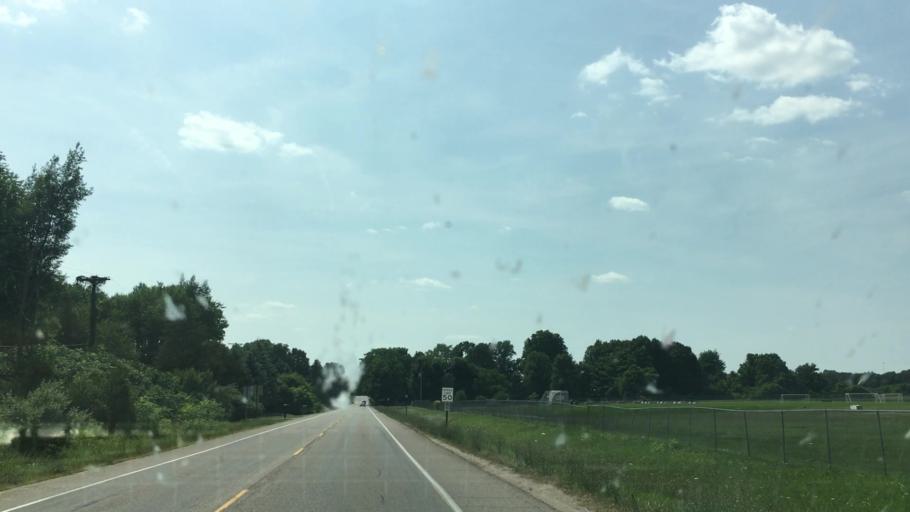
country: US
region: Michigan
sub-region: Allegan County
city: Plainwell
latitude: 42.4645
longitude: -85.6422
